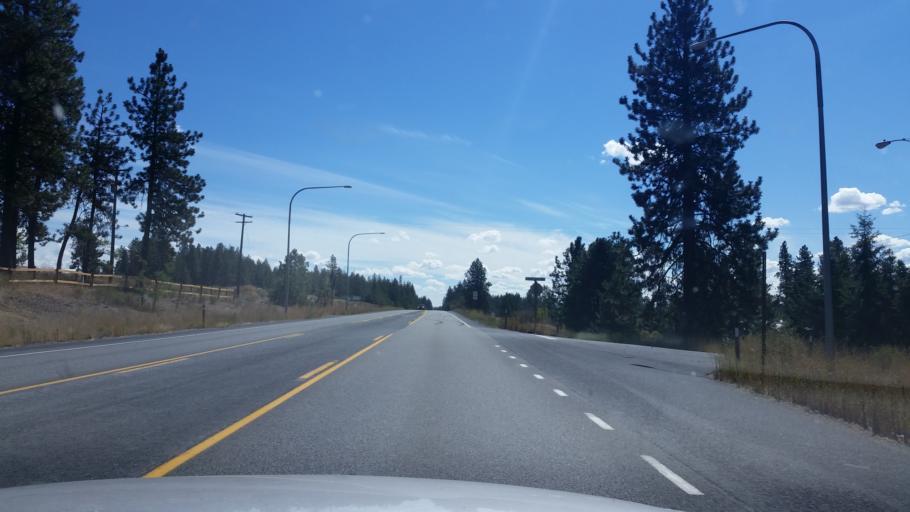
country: US
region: Washington
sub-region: Spokane County
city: Cheney
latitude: 47.5444
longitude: -117.5838
